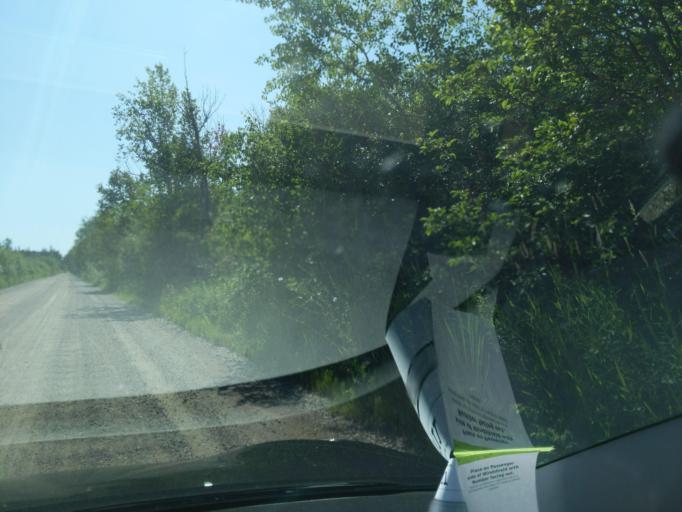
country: US
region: Michigan
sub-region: Mackinac County
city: Saint Ignace
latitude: 45.6795
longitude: -84.7004
